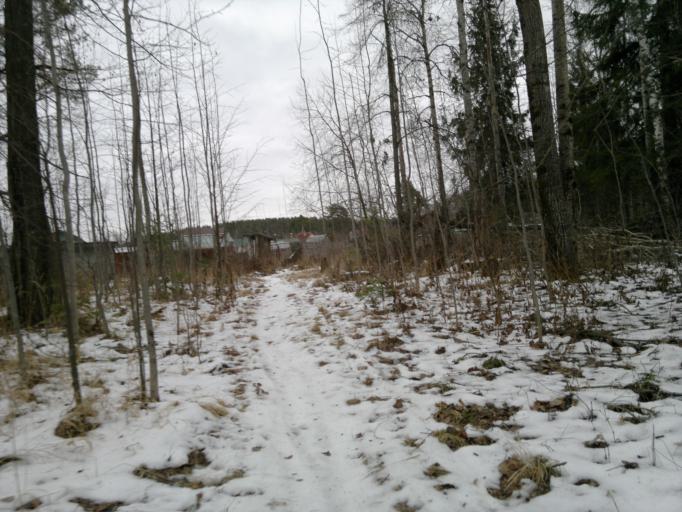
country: RU
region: Mariy-El
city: Yoshkar-Ola
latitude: 56.6105
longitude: 47.9530
